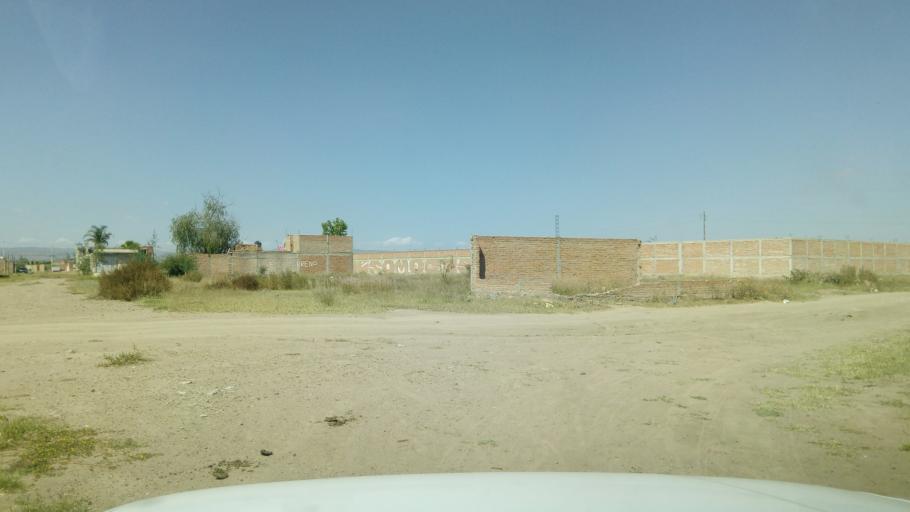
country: MX
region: Durango
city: Victoria de Durango
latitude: 23.9838
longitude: -104.6773
